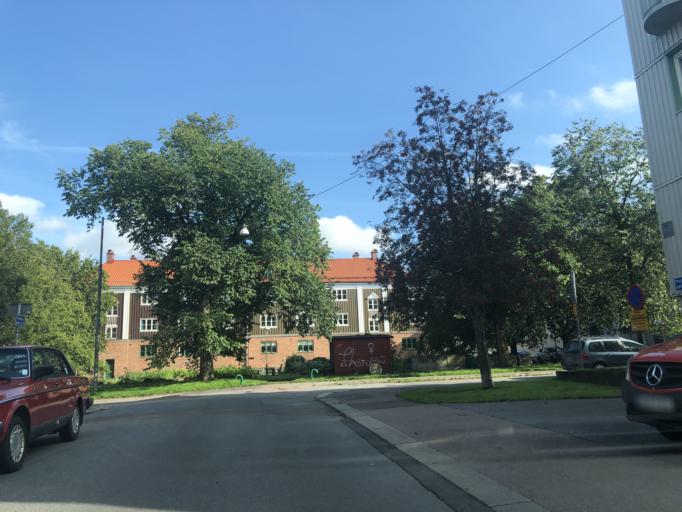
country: SE
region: Vaestra Goetaland
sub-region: Goteborg
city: Majorna
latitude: 57.6862
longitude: 11.9160
